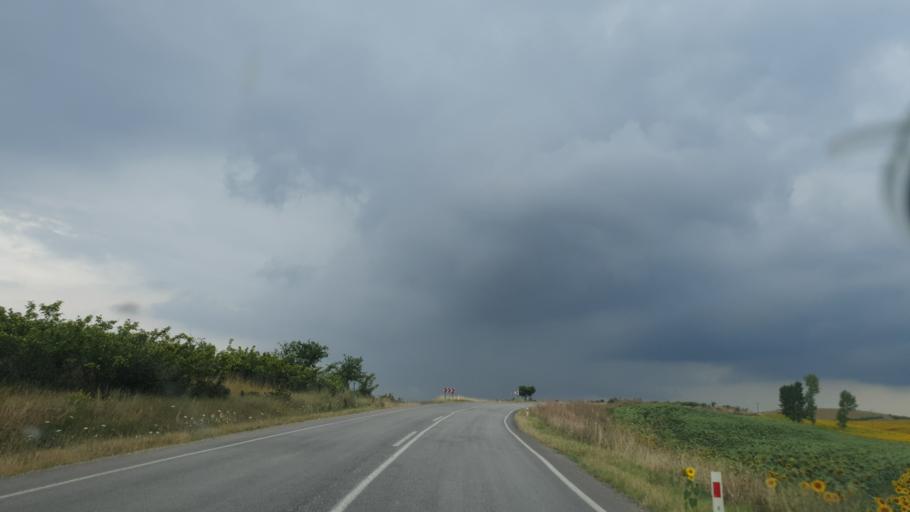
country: TR
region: Tekirdag
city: Hayrabolu
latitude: 41.2241
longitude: 27.0274
